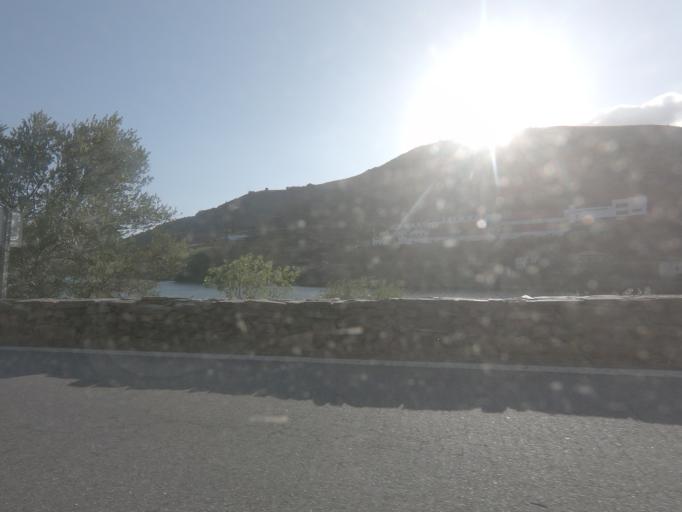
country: PT
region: Viseu
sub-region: Tabuaco
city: Tabuaco
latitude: 41.1821
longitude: -7.5498
